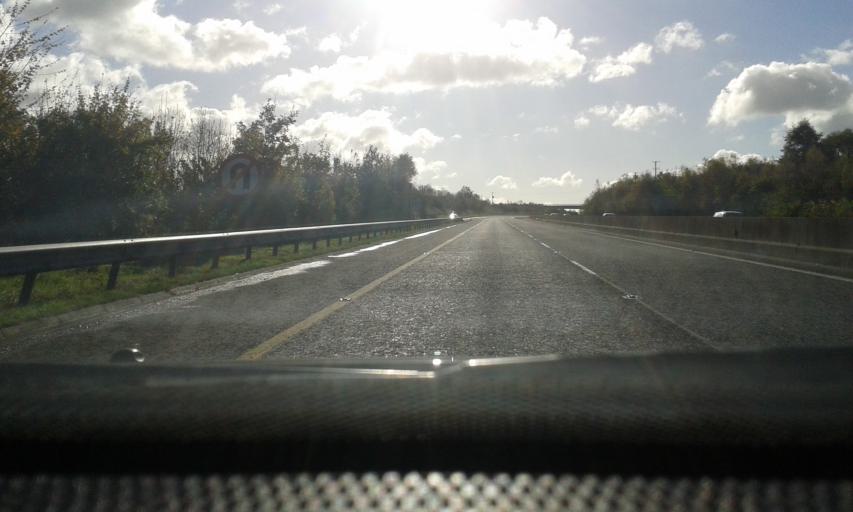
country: IE
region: Munster
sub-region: County Cork
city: Fermoy
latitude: 52.1136
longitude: -8.2731
